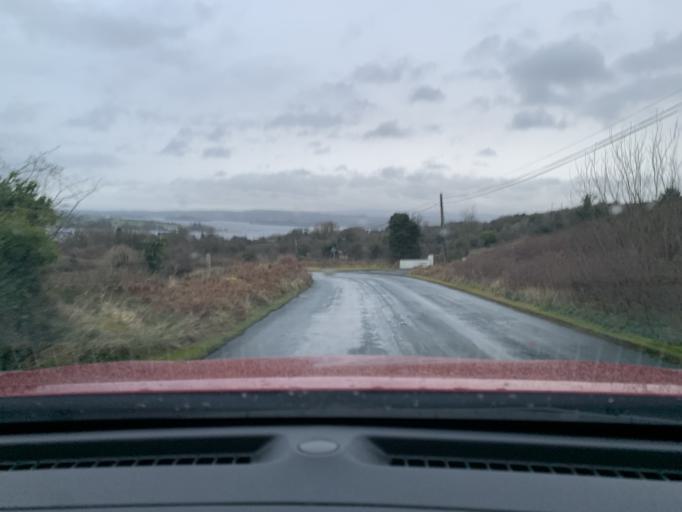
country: IE
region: Connaught
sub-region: Roscommon
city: Boyle
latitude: 54.0220
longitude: -8.3283
